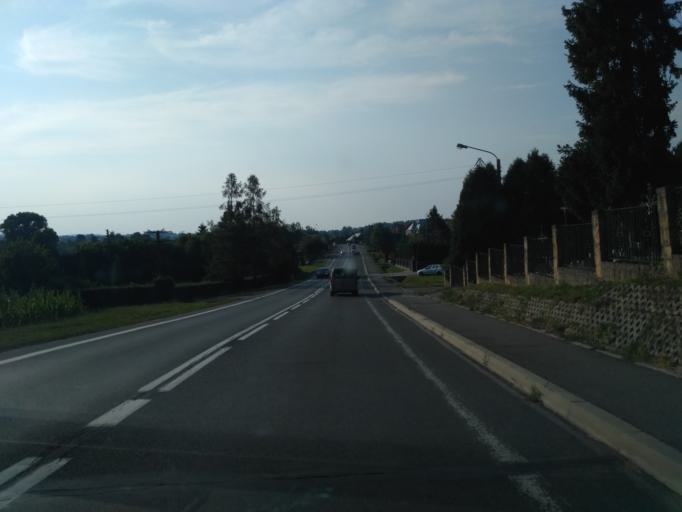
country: PL
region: Subcarpathian Voivodeship
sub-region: Powiat brzozowski
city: Humniska
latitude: 49.6728
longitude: 22.0560
